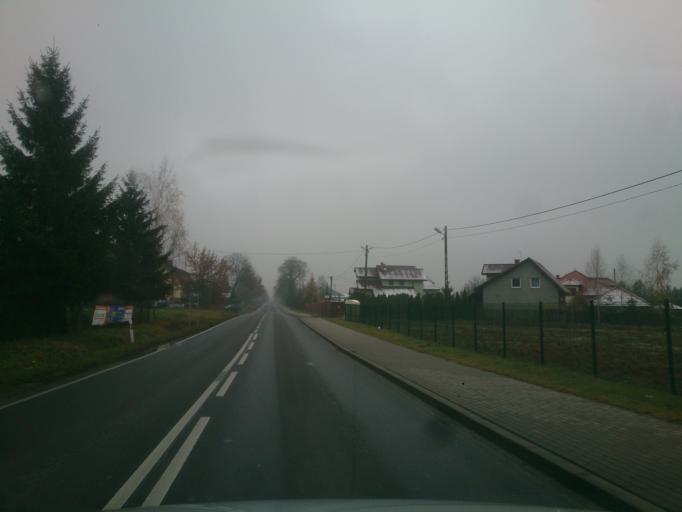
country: PL
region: Kujawsko-Pomorskie
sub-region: Powiat rypinski
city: Rypin
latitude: 53.0565
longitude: 19.4233
